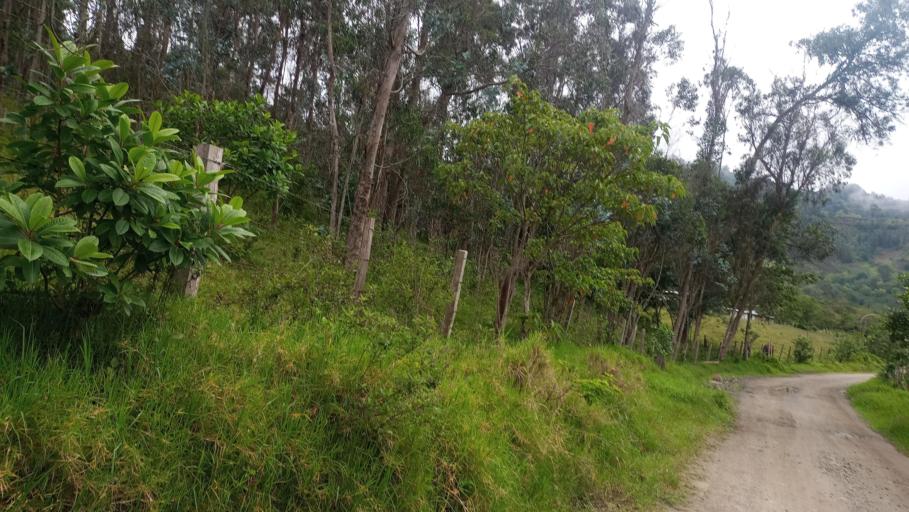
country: CO
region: Boyaca
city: Guateque
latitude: 5.0130
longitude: -73.4891
